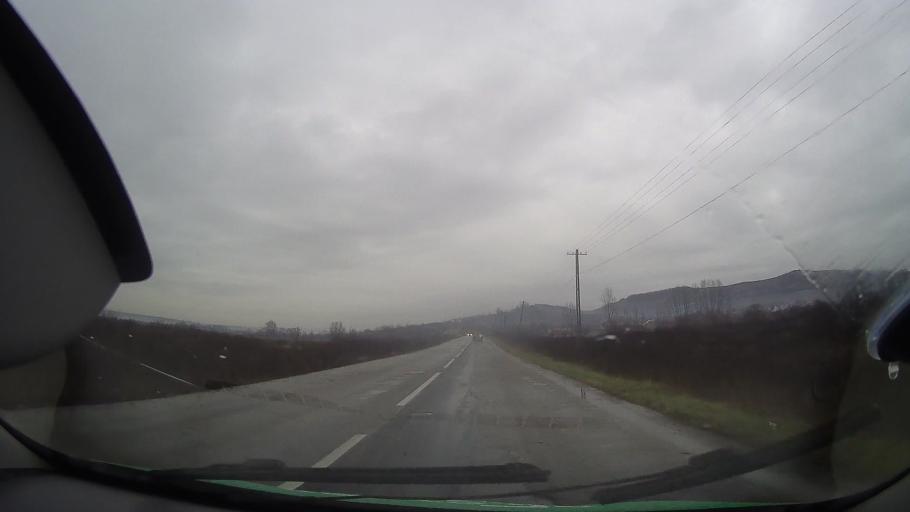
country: RO
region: Bihor
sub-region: Comuna Sambata
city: Sambata
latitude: 46.7685
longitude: 22.1860
